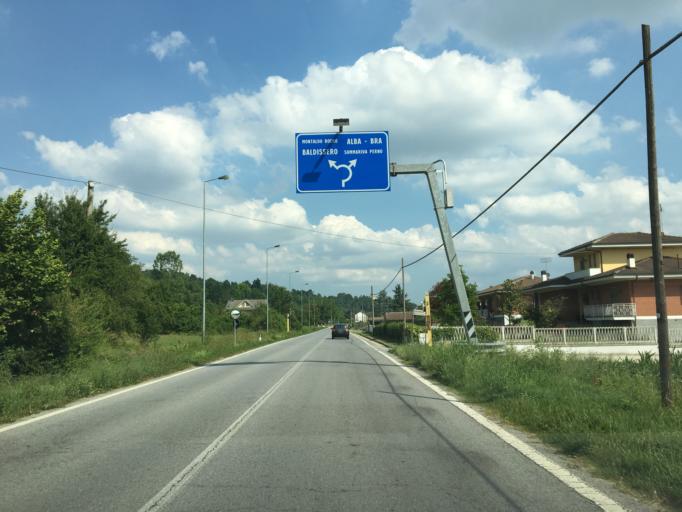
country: IT
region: Piedmont
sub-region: Provincia di Cuneo
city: Baldissero d'Alba
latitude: 44.7731
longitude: 7.8880
